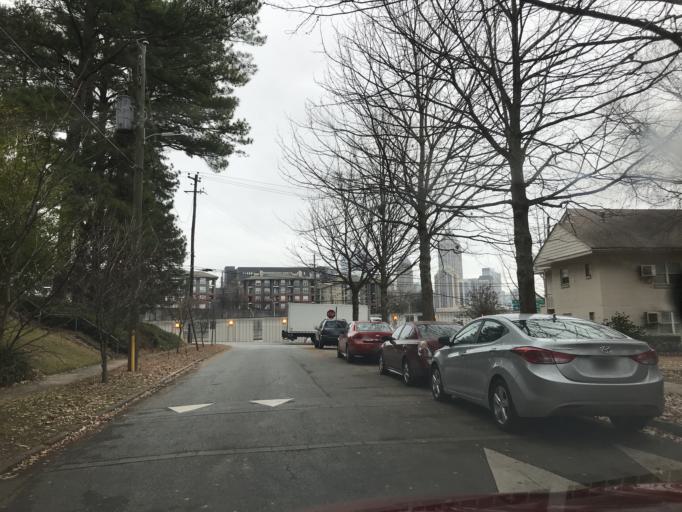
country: US
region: Georgia
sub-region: Fulton County
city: Atlanta
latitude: 33.7991
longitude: -84.3941
